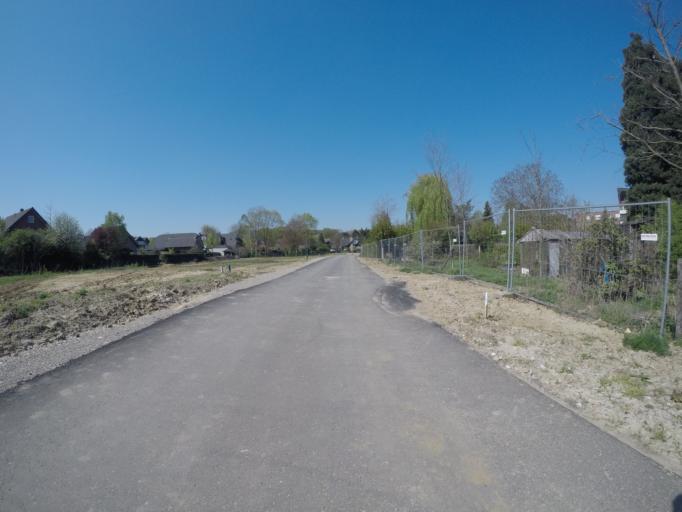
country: DE
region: North Rhine-Westphalia
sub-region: Regierungsbezirk Munster
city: Isselburg
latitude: 51.8475
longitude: 6.4338
